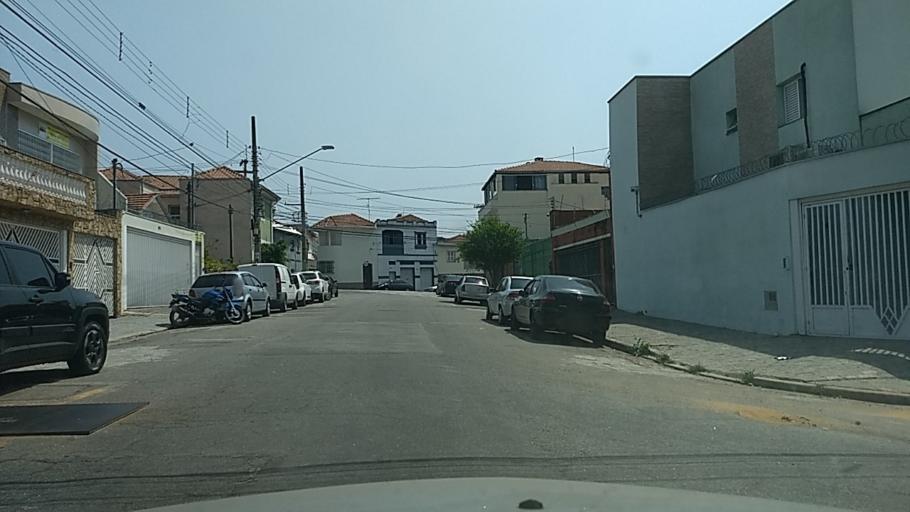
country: BR
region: Sao Paulo
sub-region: Guarulhos
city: Guarulhos
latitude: -23.5311
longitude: -46.5627
